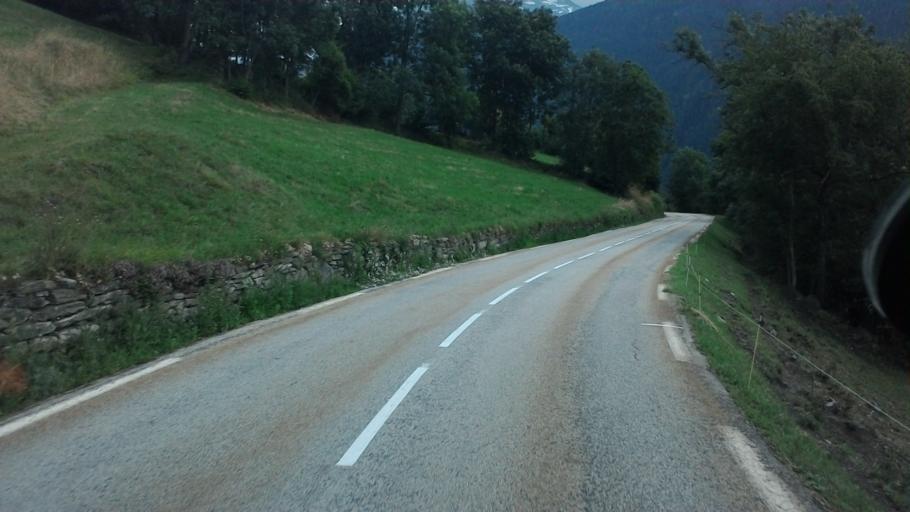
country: FR
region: Rhone-Alpes
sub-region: Departement de la Savoie
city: Seez
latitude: 45.6257
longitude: 6.8172
